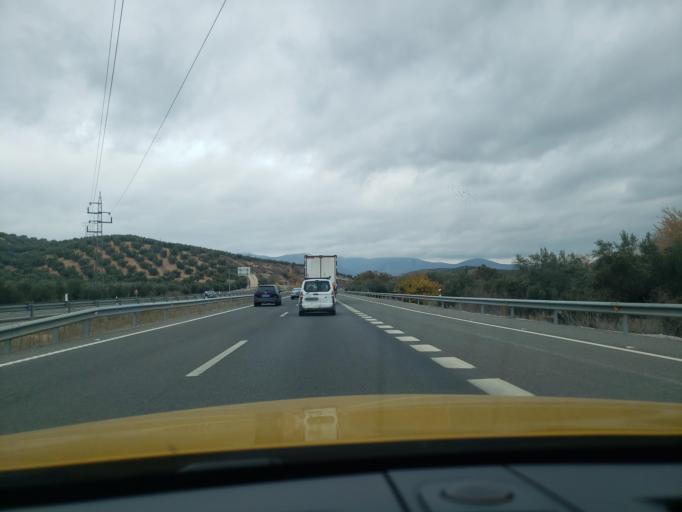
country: ES
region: Andalusia
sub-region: Provincia de Granada
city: Deifontes
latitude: 37.3274
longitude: -3.6331
